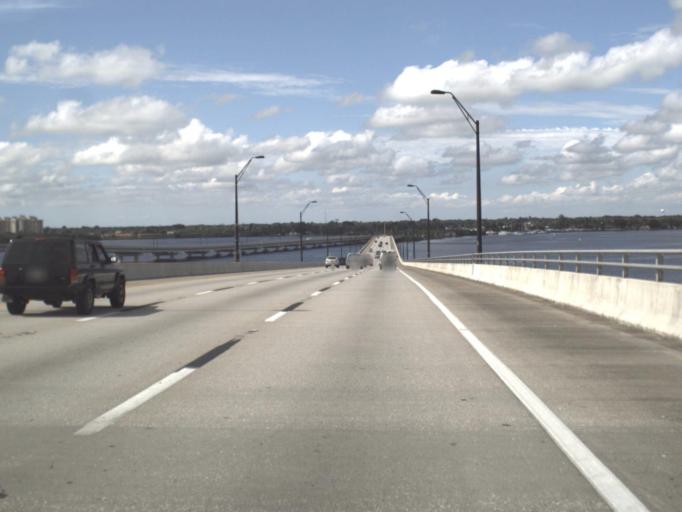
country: US
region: Florida
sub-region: Lee County
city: North Fort Myers
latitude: 26.6528
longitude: -81.8670
